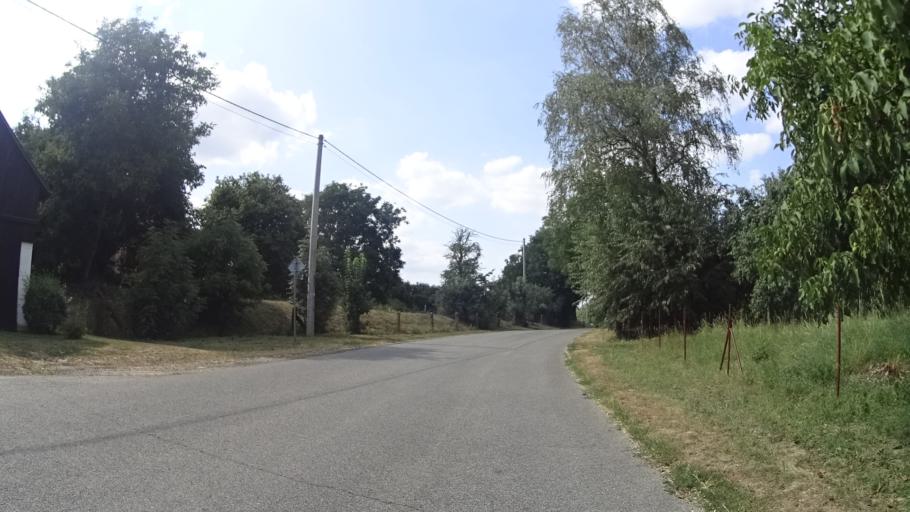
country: CZ
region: Kralovehradecky
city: Liban
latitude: 50.4047
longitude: 15.2734
